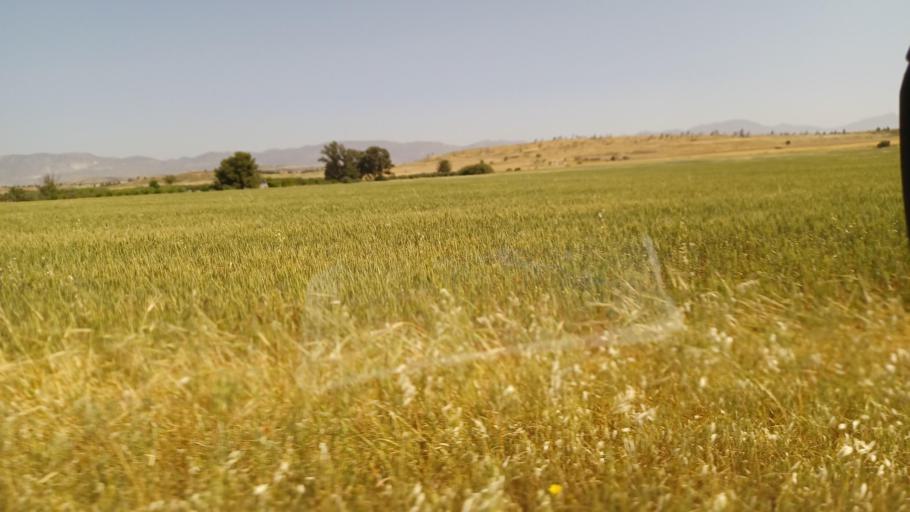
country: CY
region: Lefkosia
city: Mammari
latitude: 35.1807
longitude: 33.2127
